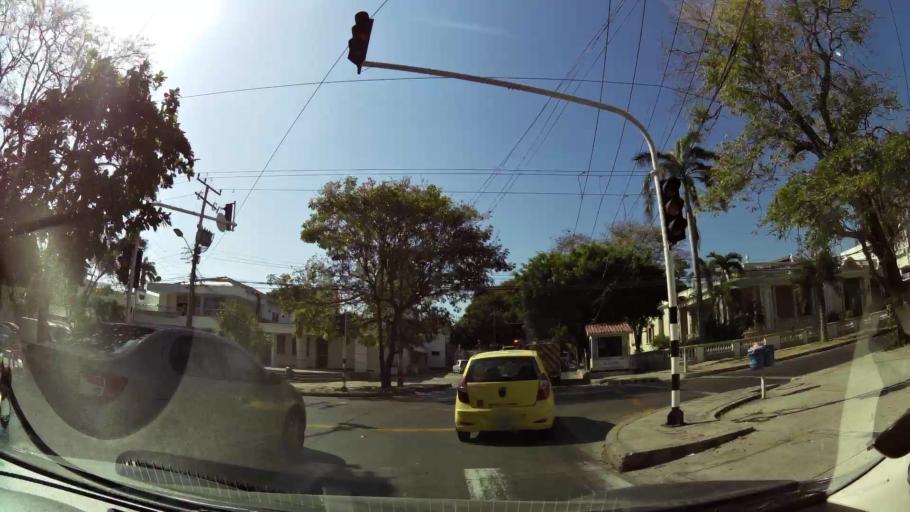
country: CO
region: Atlantico
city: Barranquilla
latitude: 10.9918
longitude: -74.7903
